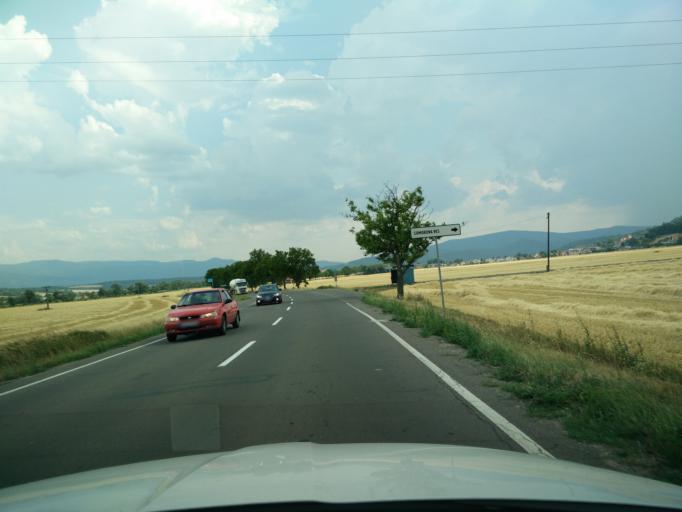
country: SK
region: Nitriansky
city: Novaky
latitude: 48.7604
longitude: 18.4966
